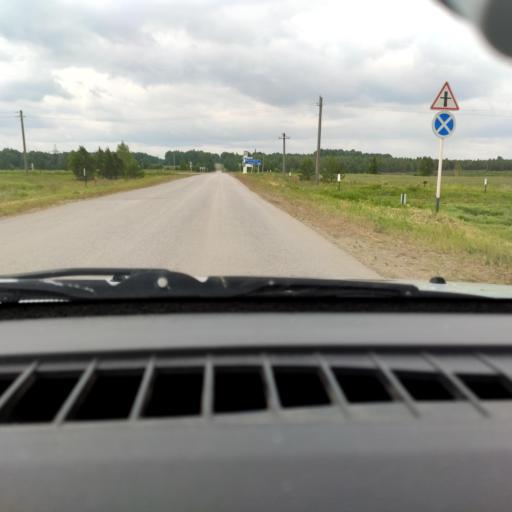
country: RU
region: Perm
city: Orda
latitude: 57.1401
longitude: 56.7263
